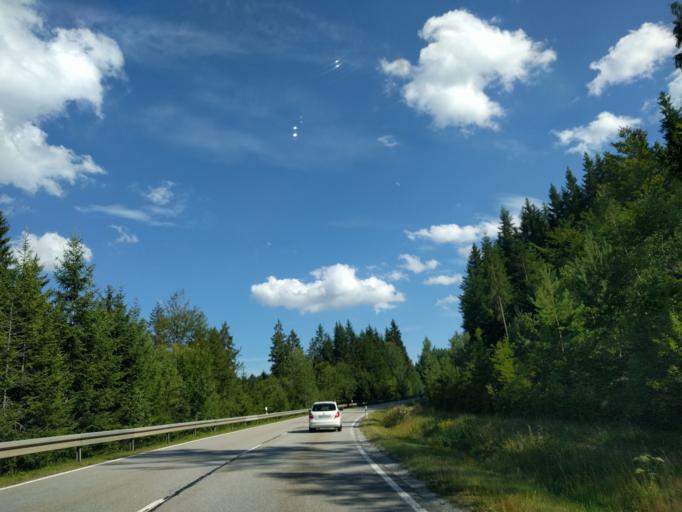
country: DE
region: Bavaria
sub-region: Lower Bavaria
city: Langdorf
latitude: 49.0214
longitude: 13.1370
